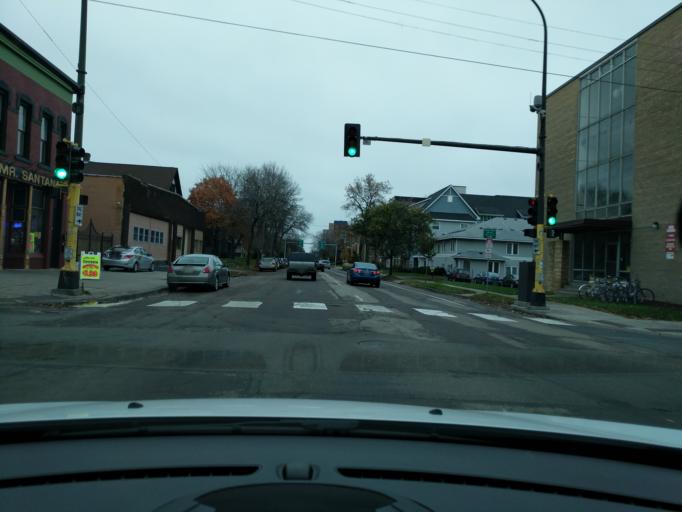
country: US
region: Minnesota
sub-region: Hennepin County
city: Minneapolis
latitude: 44.9840
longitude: -93.2479
